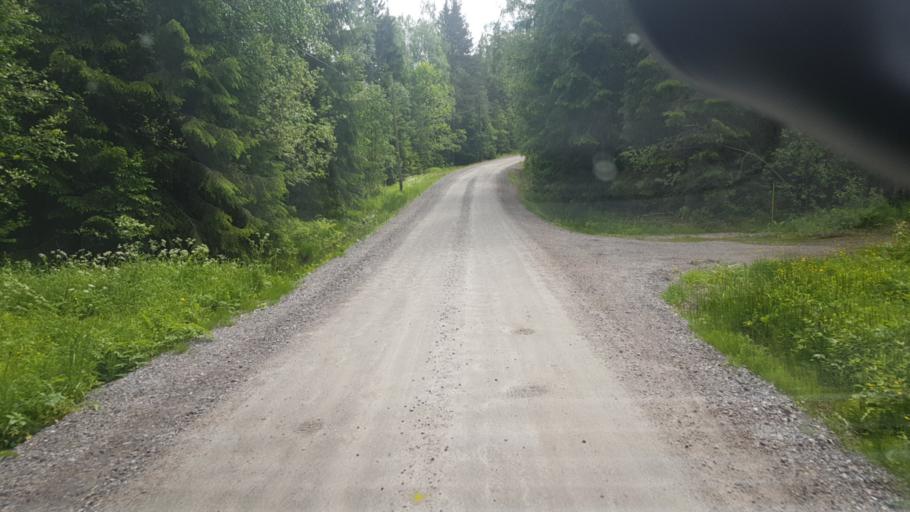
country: SE
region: Vaermland
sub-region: Eda Kommun
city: Charlottenberg
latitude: 59.9130
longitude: 12.3849
